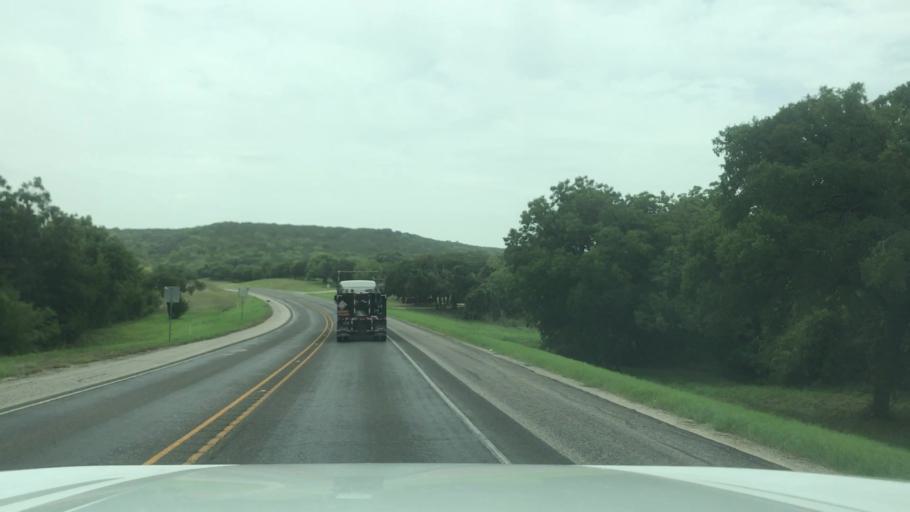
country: US
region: Texas
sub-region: Bosque County
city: Meridian
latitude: 31.9067
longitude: -97.6611
